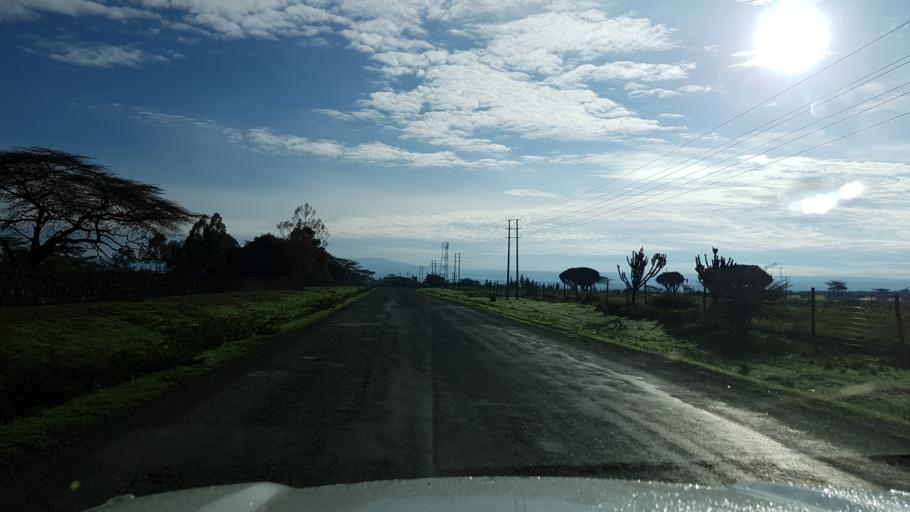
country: KE
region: Nakuru
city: Naivasha
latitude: -0.8179
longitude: 36.3920
